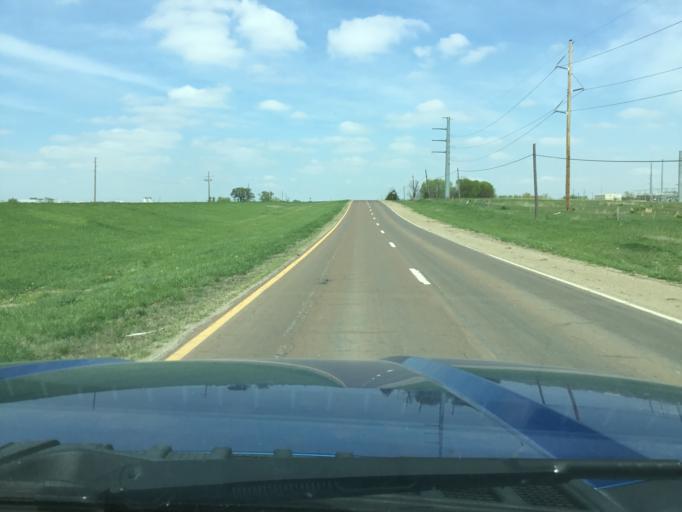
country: US
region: Kansas
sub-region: Osage County
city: Carbondale
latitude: 38.9239
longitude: -95.6875
